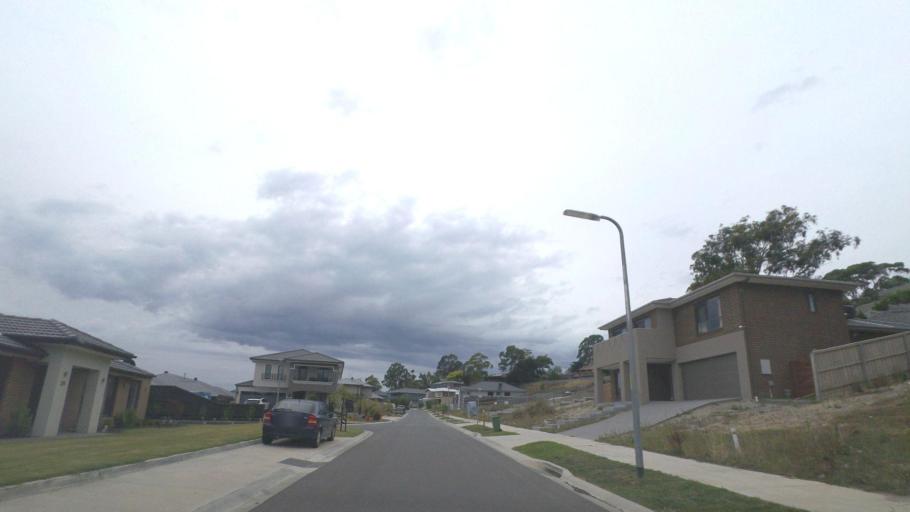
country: AU
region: Victoria
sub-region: Yarra Ranges
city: Chirnside Park
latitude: -37.7518
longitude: 145.3223
